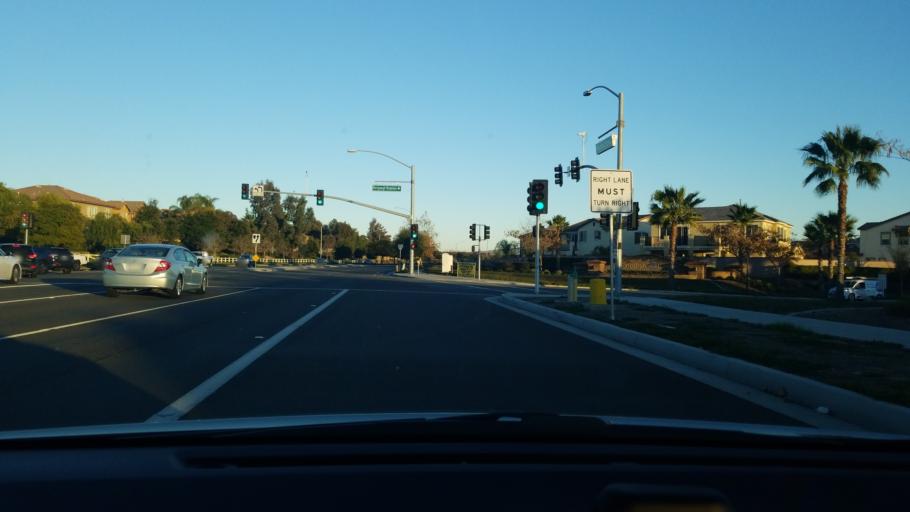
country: US
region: California
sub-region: Riverside County
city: Murrieta Hot Springs
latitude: 33.5542
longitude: -117.1114
